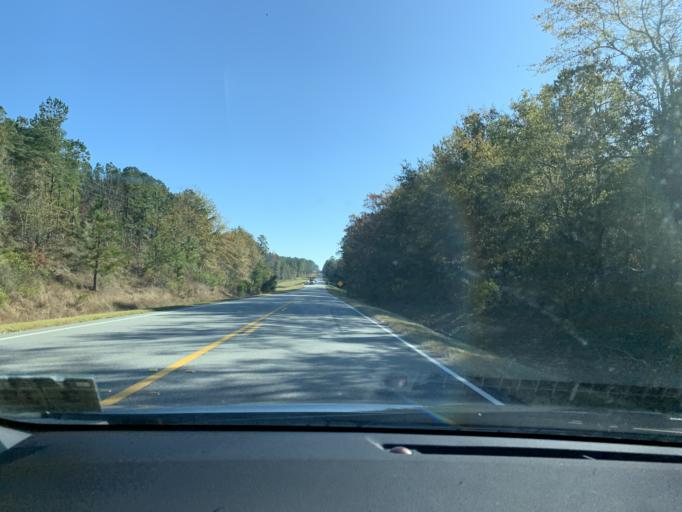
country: US
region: Georgia
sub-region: Ben Hill County
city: Fitzgerald
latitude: 31.7743
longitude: -83.0570
